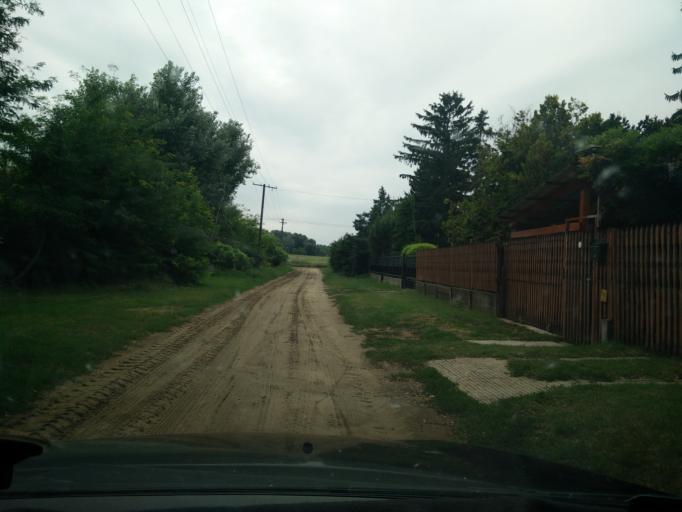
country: HU
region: Hajdu-Bihar
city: Debrecen
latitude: 47.5225
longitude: 21.7134
